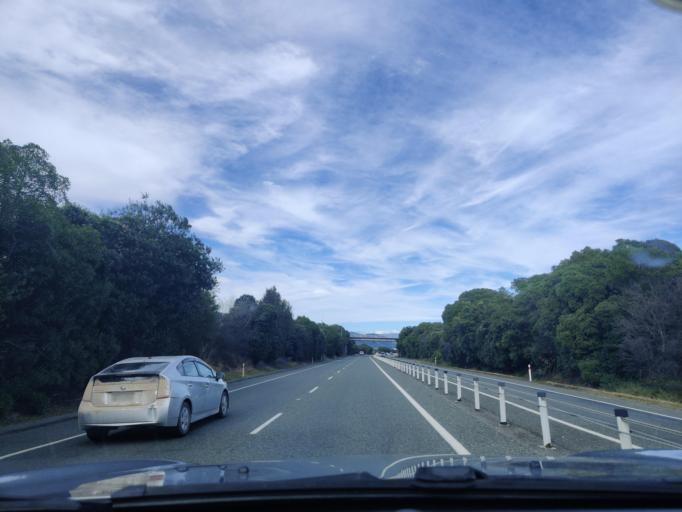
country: NZ
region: Tasman
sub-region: Tasman District
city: Richmond
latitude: -41.3053
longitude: 173.2228
